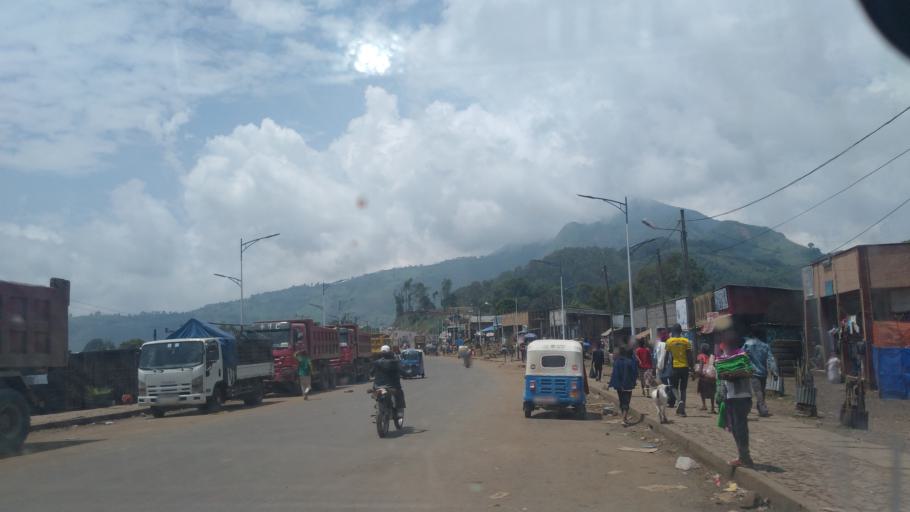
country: ET
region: Southern Nations, Nationalities, and People's Region
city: Bonga
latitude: 7.1066
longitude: 36.6768
